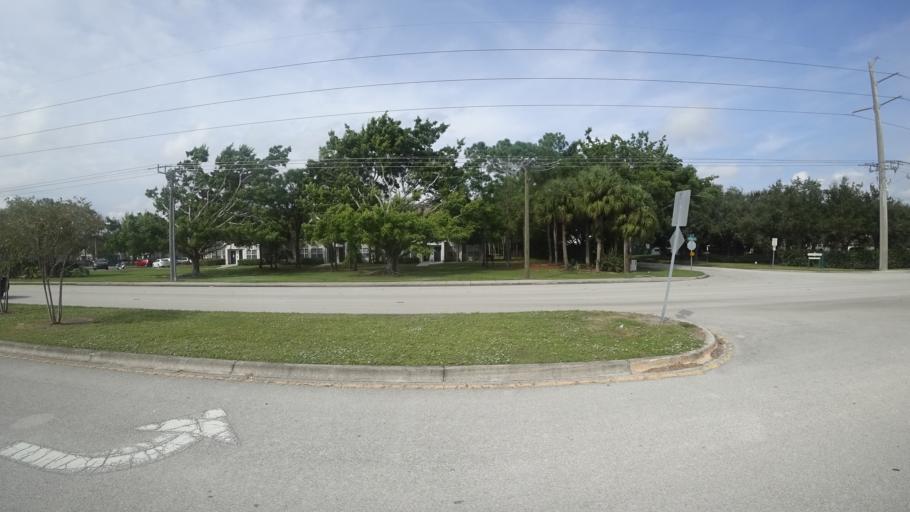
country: US
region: Florida
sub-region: Manatee County
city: Bayshore Gardens
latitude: 27.4478
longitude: -82.6035
